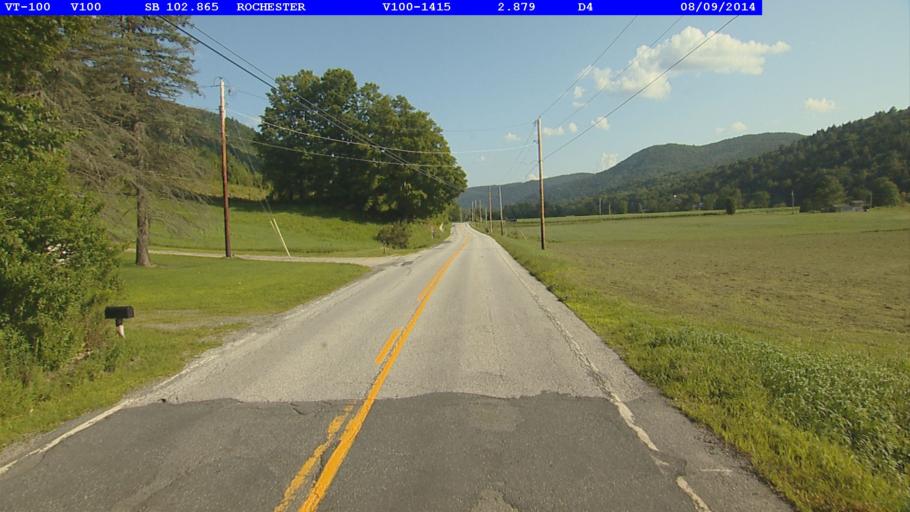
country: US
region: Vermont
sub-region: Orange County
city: Randolph
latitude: 43.8432
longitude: -72.7982
